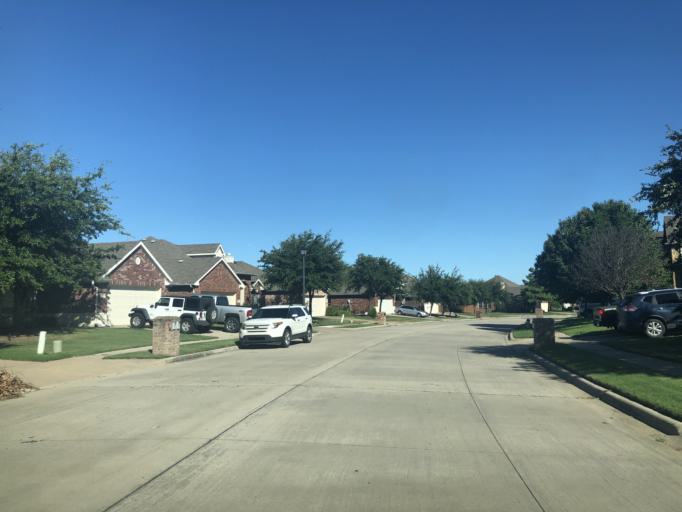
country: US
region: Texas
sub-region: Dallas County
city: Duncanville
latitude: 32.6594
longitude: -96.9670
